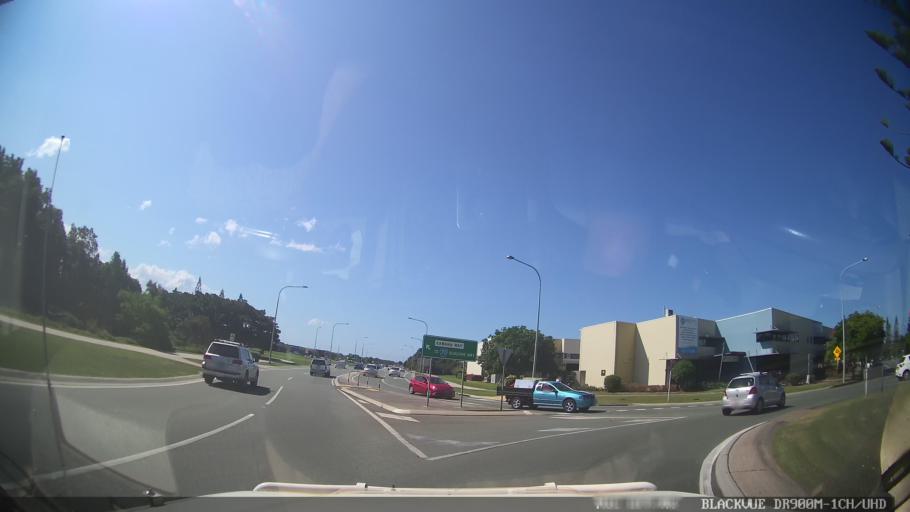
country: AU
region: Queensland
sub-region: Sunshine Coast
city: Mooloolaba
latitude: -26.7318
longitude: 153.1205
